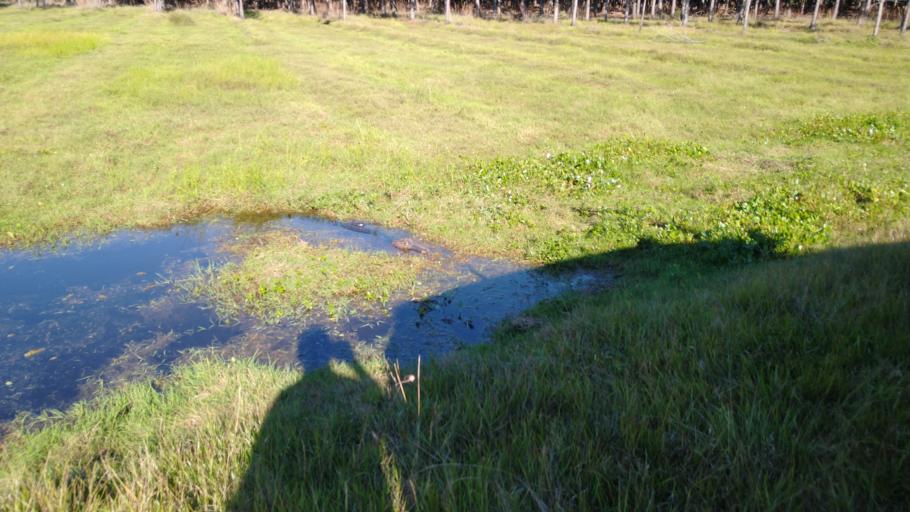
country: AR
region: Corrientes
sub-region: Departamento de San Miguel
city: San Miguel
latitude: -28.1869
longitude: -57.5561
